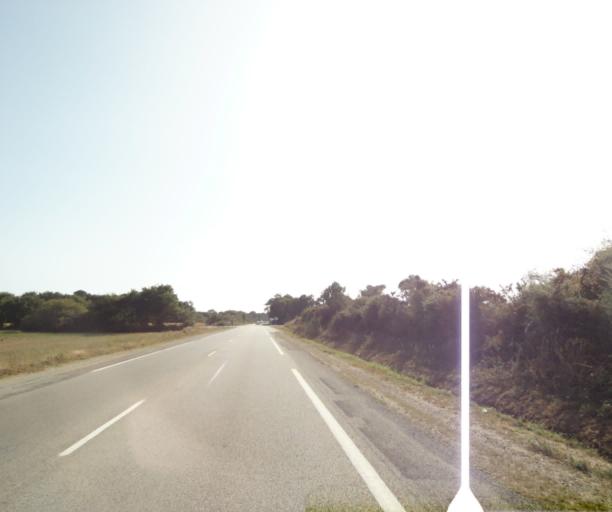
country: FR
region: Brittany
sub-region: Departement du Morbihan
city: Riantec
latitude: 47.7412
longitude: -3.3018
